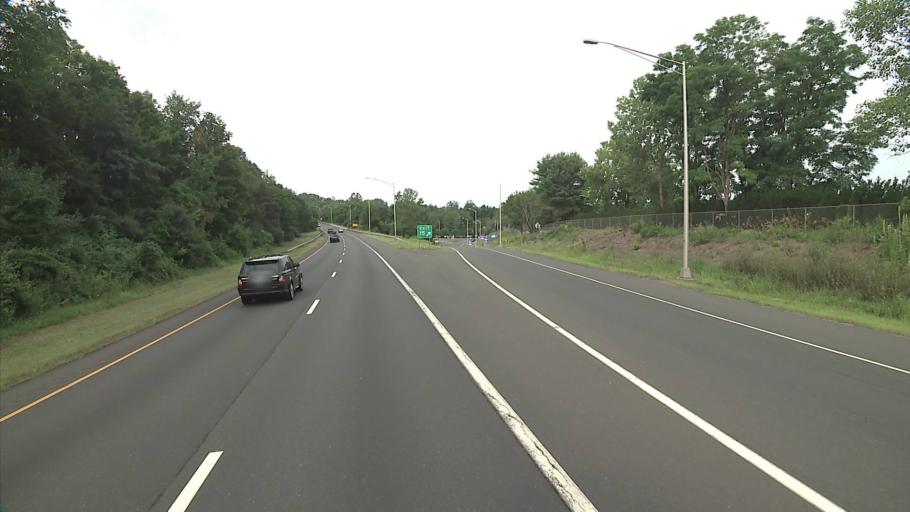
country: US
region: Connecticut
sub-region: New Haven County
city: Southbury
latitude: 41.4782
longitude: -73.2090
